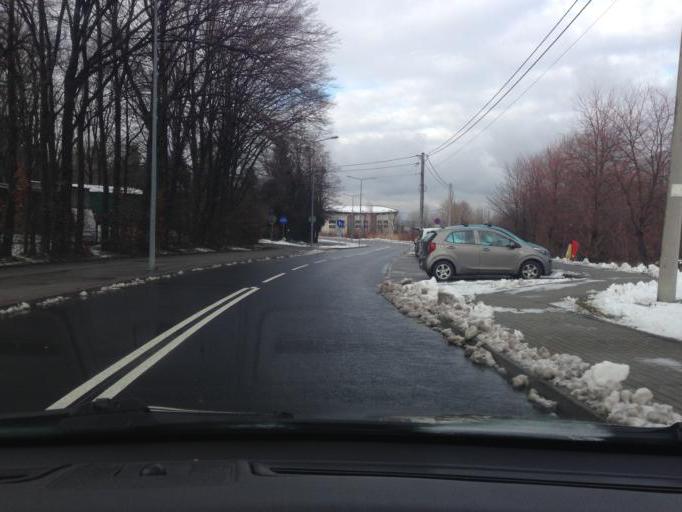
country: PL
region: Silesian Voivodeship
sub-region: Powiat bielski
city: Bystra
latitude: 49.7818
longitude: 19.0233
